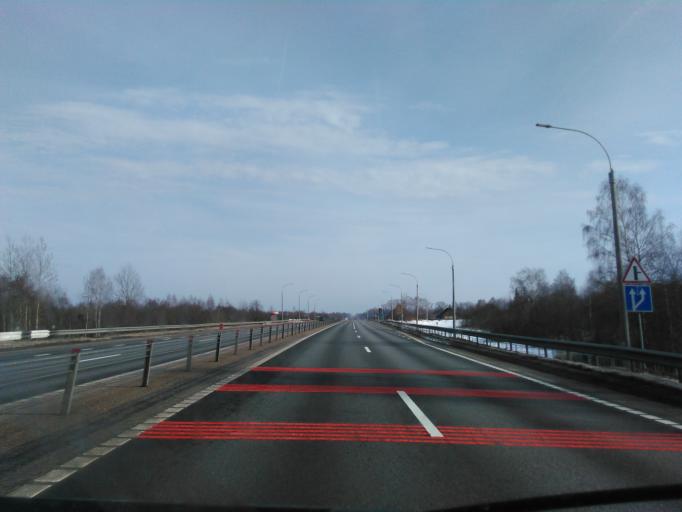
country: BY
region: Vitebsk
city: Dubrowna
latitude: 54.6893
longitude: 30.8854
